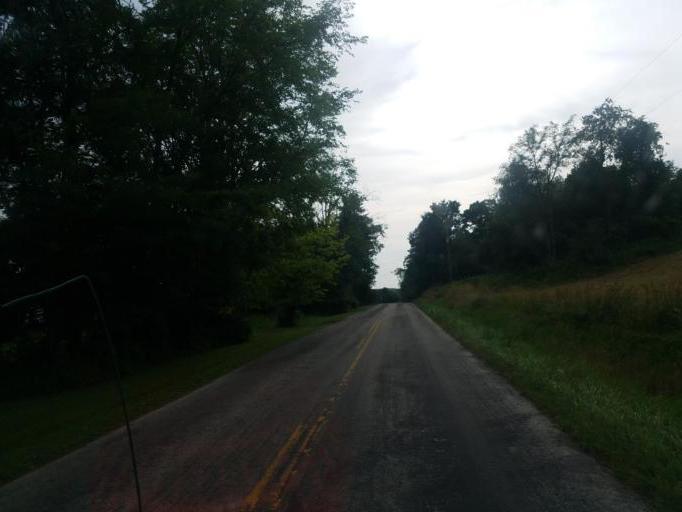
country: US
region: Ohio
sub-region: Wayne County
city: West Salem
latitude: 40.9009
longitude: -82.1454
